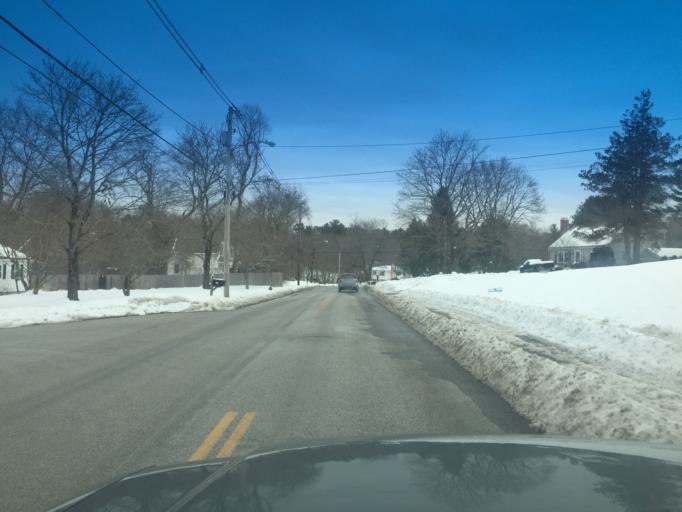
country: US
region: Massachusetts
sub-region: Norfolk County
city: Foxborough
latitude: 42.1019
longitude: -71.2780
